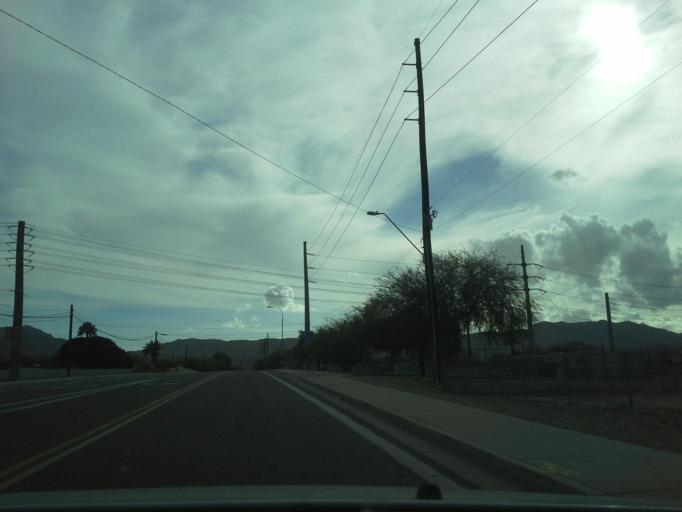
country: US
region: Arizona
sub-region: Maricopa County
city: Phoenix
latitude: 33.3775
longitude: -112.0834
